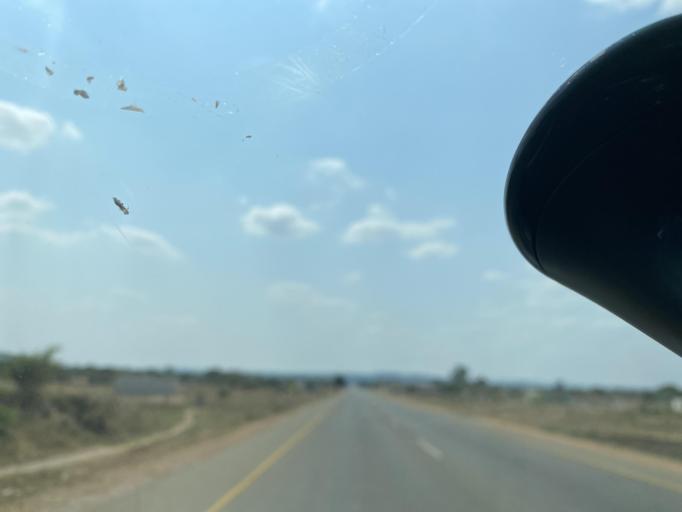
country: ZM
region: Lusaka
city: Chongwe
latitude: -15.5683
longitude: 28.6932
